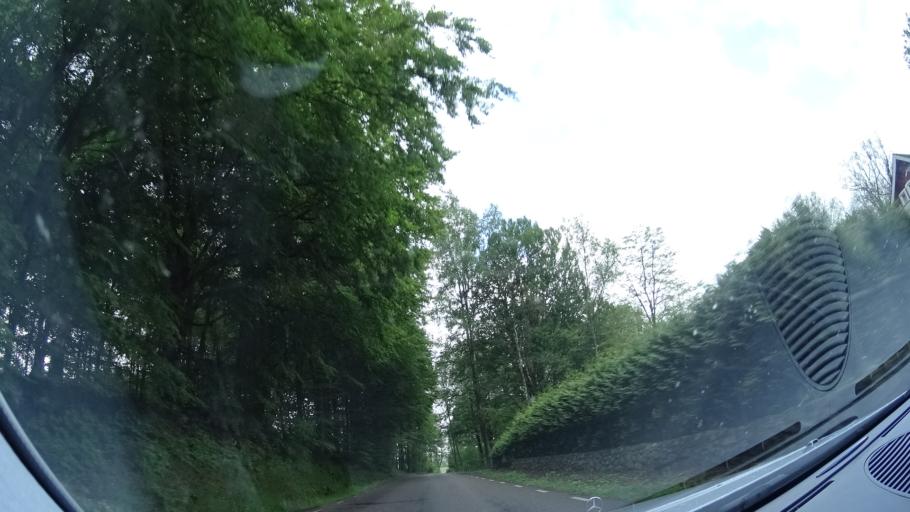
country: SE
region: Skane
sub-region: Hoors Kommun
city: Hoeoer
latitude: 55.9551
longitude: 13.4530
